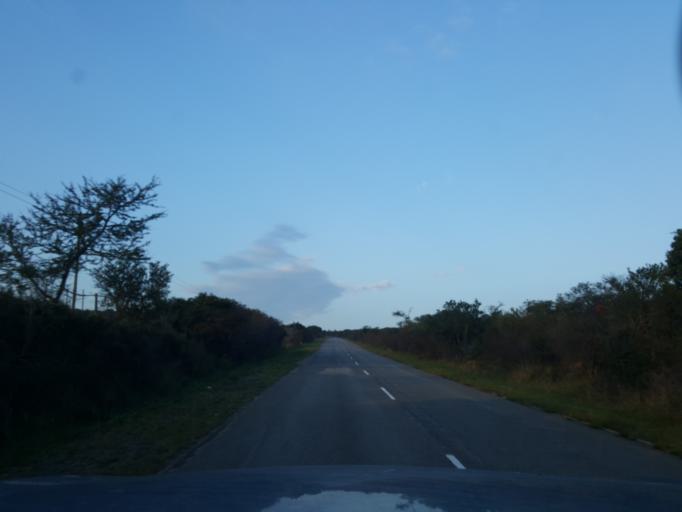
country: ZA
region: Eastern Cape
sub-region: Cacadu District Municipality
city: Grahamstown
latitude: -33.4623
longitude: 26.4885
